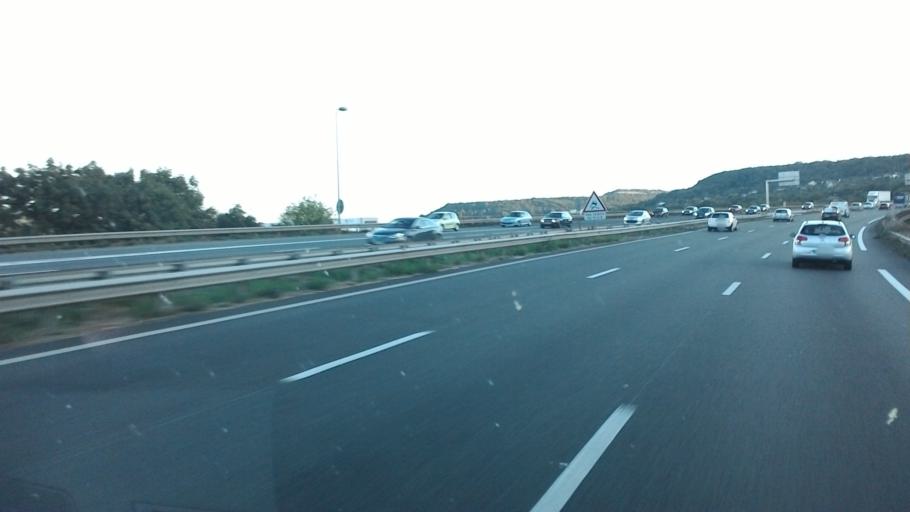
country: FR
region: Lorraine
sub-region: Departement de Meurthe-et-Moselle
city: Bouxieres-aux-Dames
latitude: 48.7502
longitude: 6.1566
